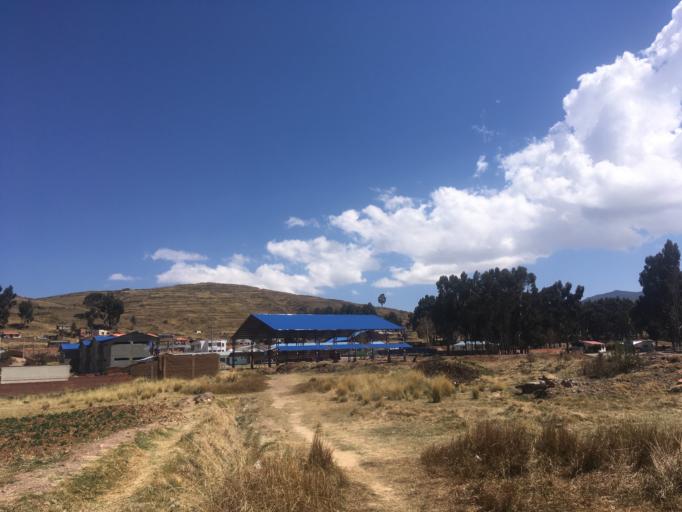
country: BO
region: La Paz
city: Huatajata
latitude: -16.1912
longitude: -68.7478
